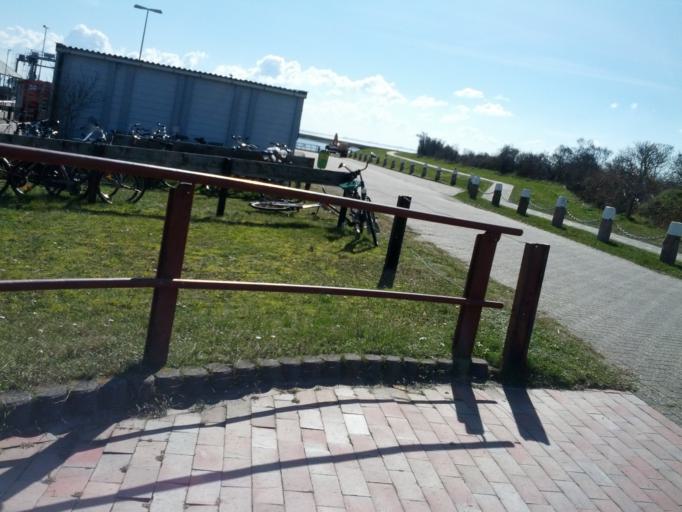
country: DE
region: Lower Saxony
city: Langeoog
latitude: 53.7260
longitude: 7.4938
